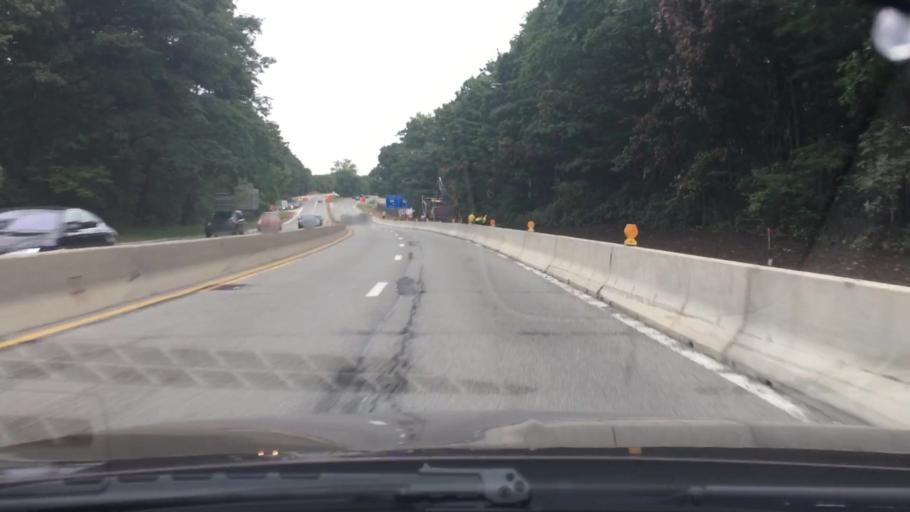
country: US
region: New York
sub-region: Suffolk County
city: Dix Hills
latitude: 40.8240
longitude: -73.3414
